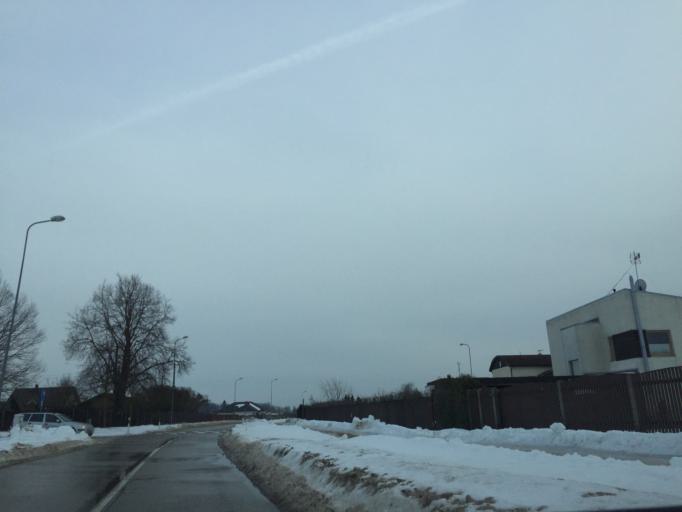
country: LV
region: Ikskile
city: Ikskile
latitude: 56.8375
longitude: 24.4770
